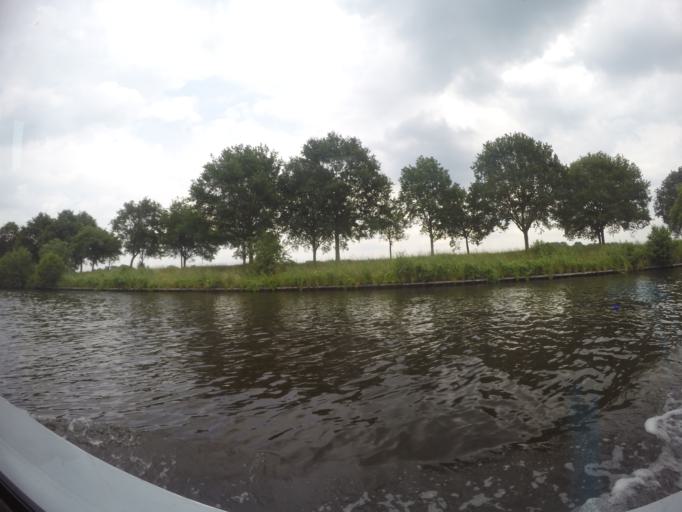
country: NL
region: Overijssel
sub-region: Gemeente Hof van Twente
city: Delden
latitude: 52.2684
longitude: 6.6444
